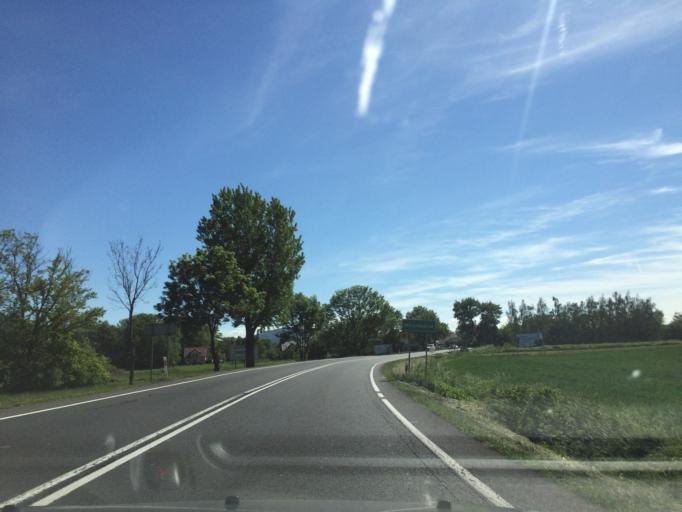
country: PL
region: Lower Silesian Voivodeship
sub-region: Powiat wroclawski
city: Gniechowice
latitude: 50.9588
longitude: 16.7865
